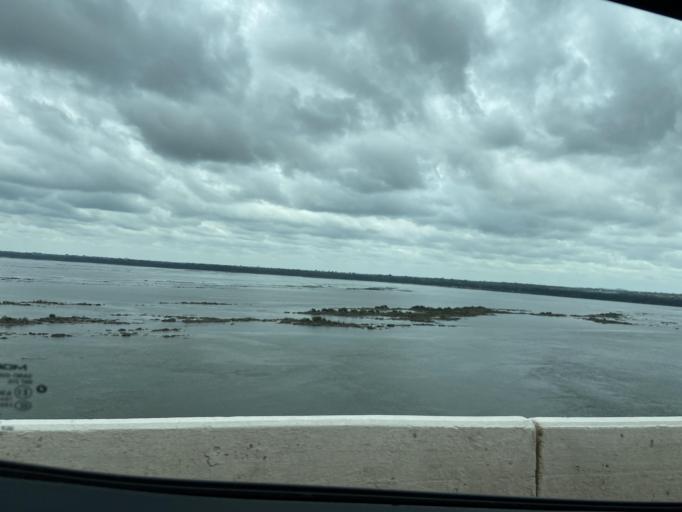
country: BR
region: Para
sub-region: Maraba
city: Maraba
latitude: -5.3198
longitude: -49.0823
